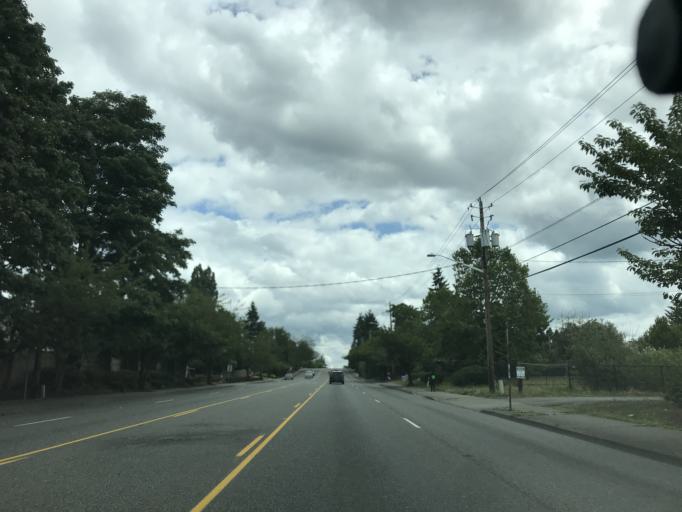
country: US
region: Washington
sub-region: King County
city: Fairwood
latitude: 47.4452
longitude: -122.1940
